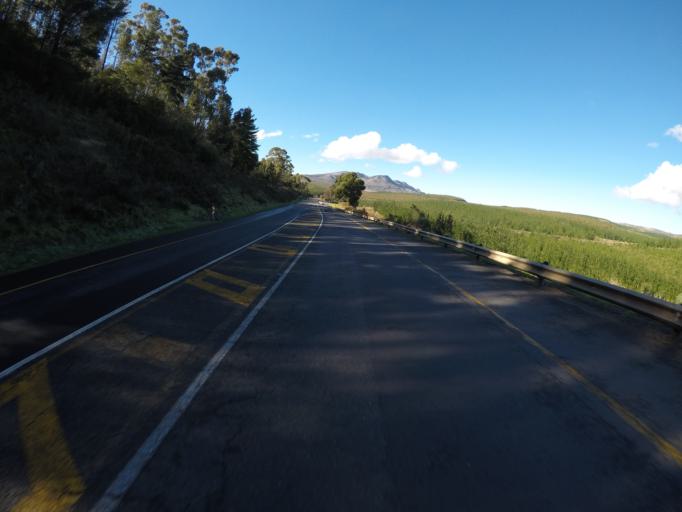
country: ZA
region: Western Cape
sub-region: Overberg District Municipality
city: Grabouw
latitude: -34.1937
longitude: 19.1031
